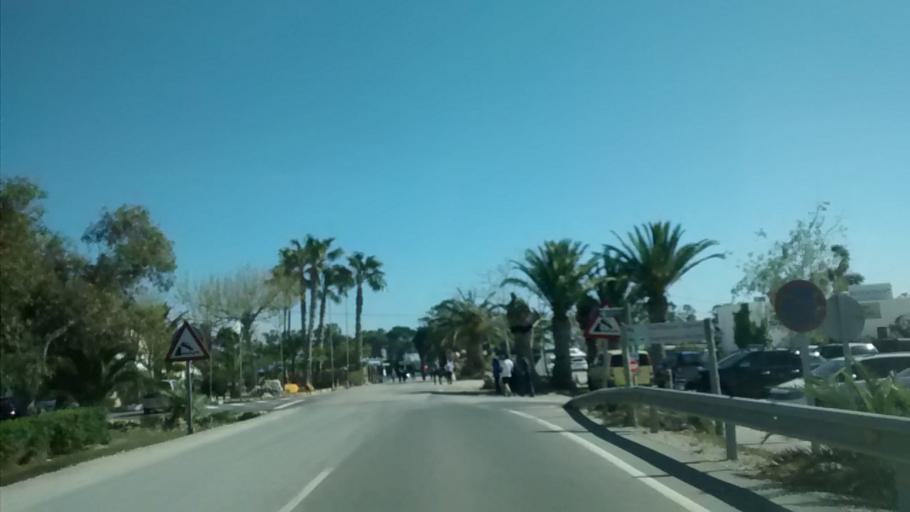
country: ES
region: Catalonia
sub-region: Provincia de Tarragona
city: Deltebre
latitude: 40.7138
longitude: 0.8341
